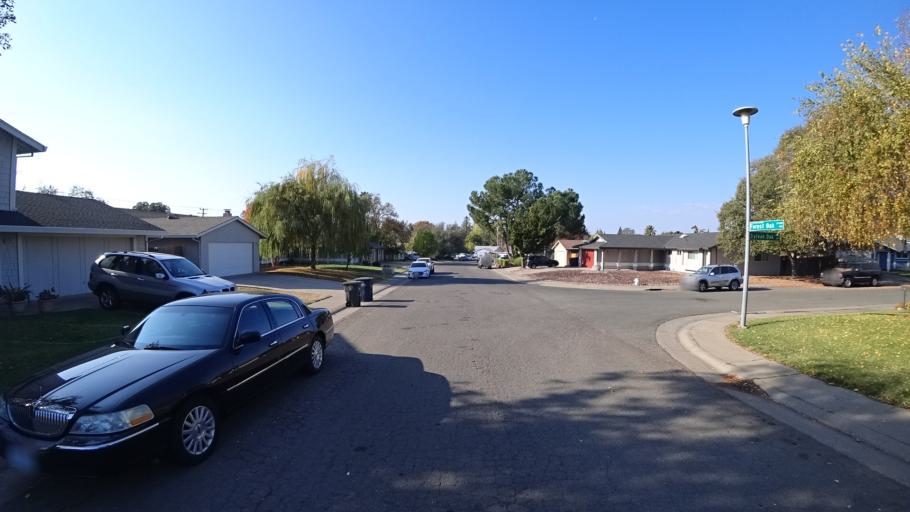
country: US
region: California
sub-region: Sacramento County
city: Citrus Heights
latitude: 38.7095
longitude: -121.2607
